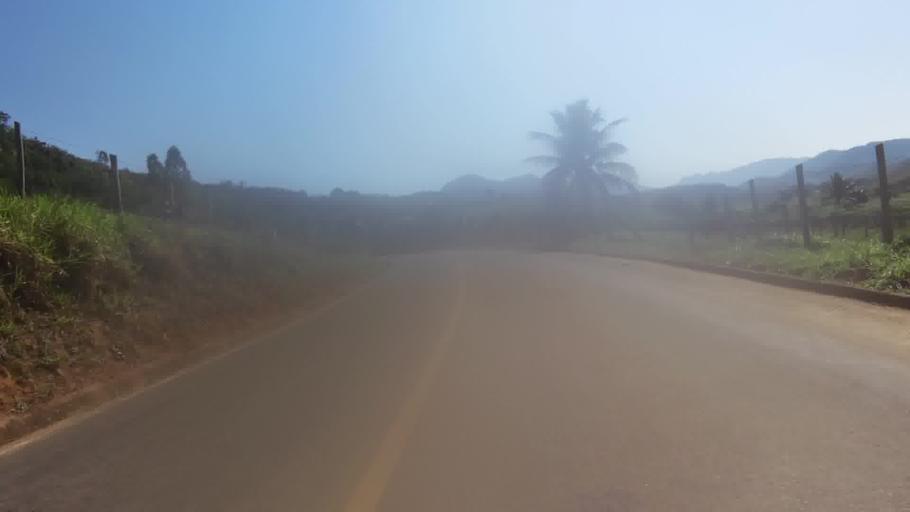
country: BR
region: Espirito Santo
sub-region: Alfredo Chaves
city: Alfredo Chaves
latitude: -20.6637
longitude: -40.7645
